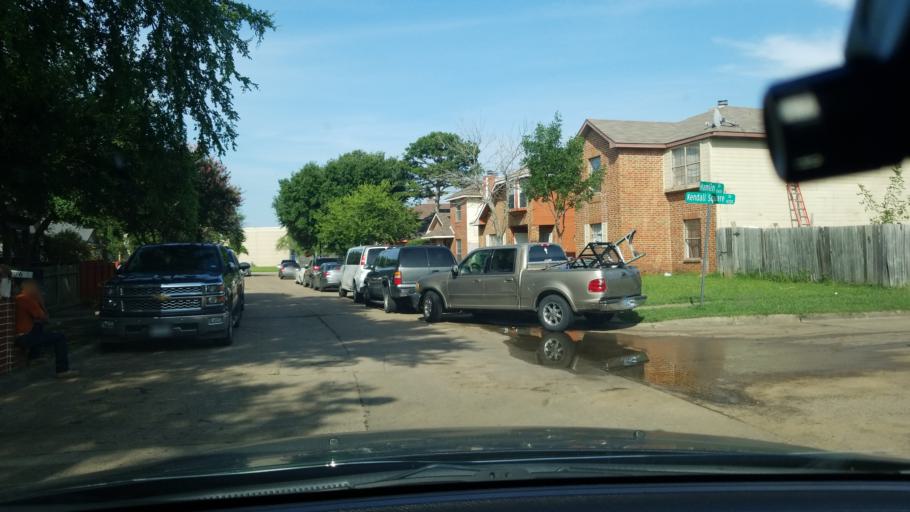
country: US
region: Texas
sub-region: Dallas County
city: Balch Springs
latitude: 32.7181
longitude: -96.6413
